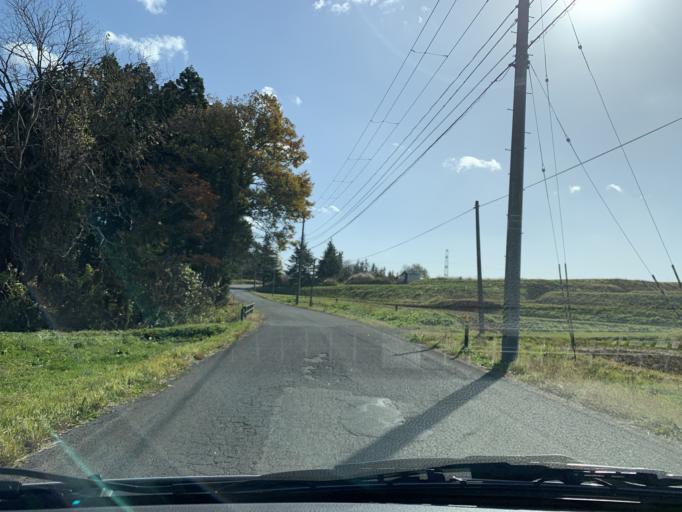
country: JP
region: Iwate
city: Mizusawa
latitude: 39.0285
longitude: 141.1217
